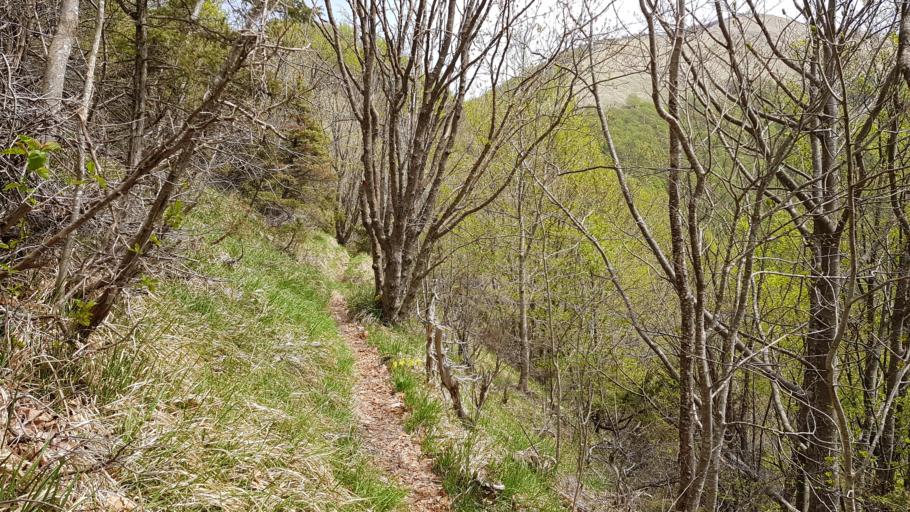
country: IT
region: Liguria
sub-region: Provincia di Genova
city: Gorreto
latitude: 44.6295
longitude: 9.2583
